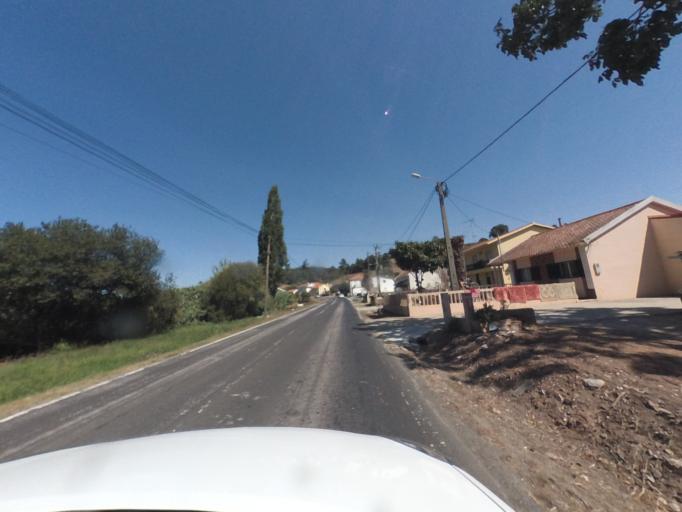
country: PT
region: Leiria
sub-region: Alcobaca
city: Alcobaca
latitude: 39.5285
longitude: -8.9952
